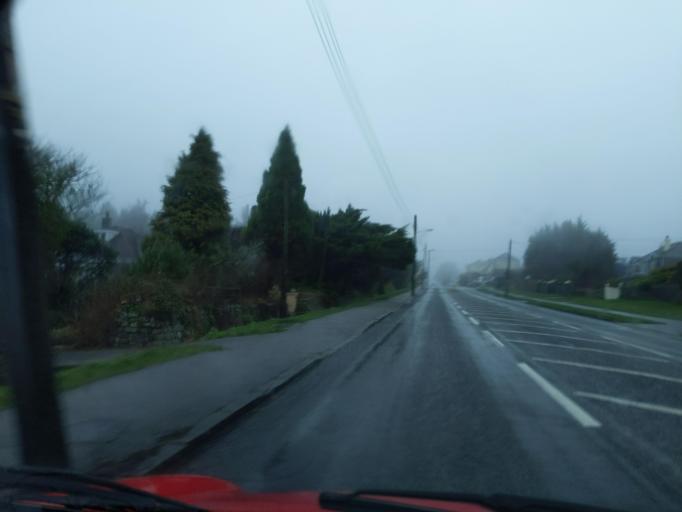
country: GB
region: England
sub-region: Cornwall
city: Callington
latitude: 50.5179
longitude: -4.3156
